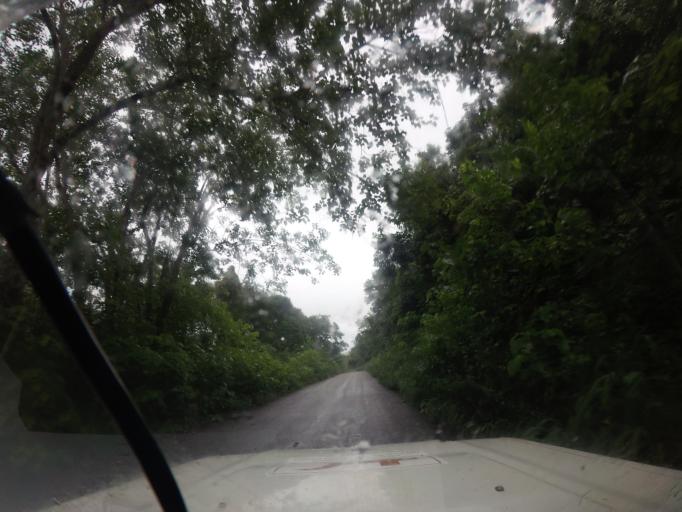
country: SL
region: Northern Province
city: Kabala
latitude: 9.4357
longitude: -11.7144
